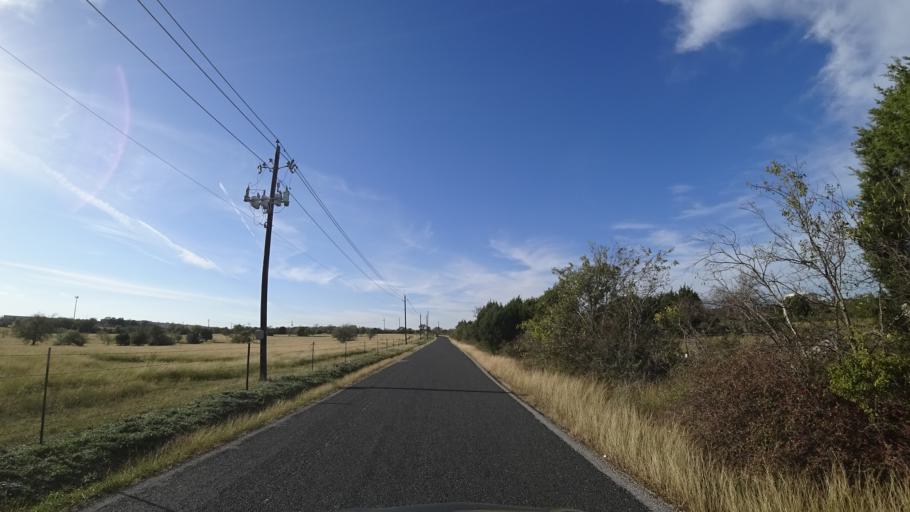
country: US
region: Texas
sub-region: Travis County
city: Wells Branch
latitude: 30.4491
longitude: -97.6998
